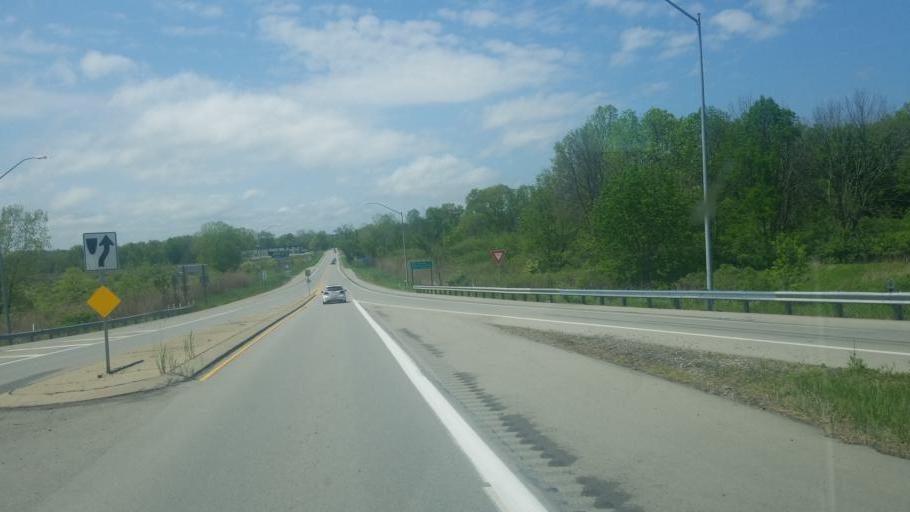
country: US
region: Pennsylvania
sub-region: Mercer County
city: Hermitage
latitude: 41.1878
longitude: -80.4573
